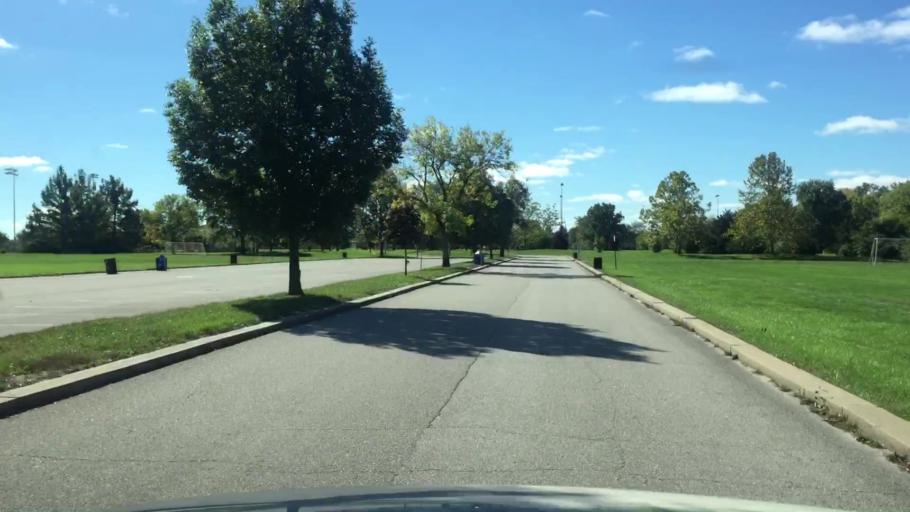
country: US
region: Missouri
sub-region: Boone County
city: Columbia
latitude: 38.9744
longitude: -92.3635
